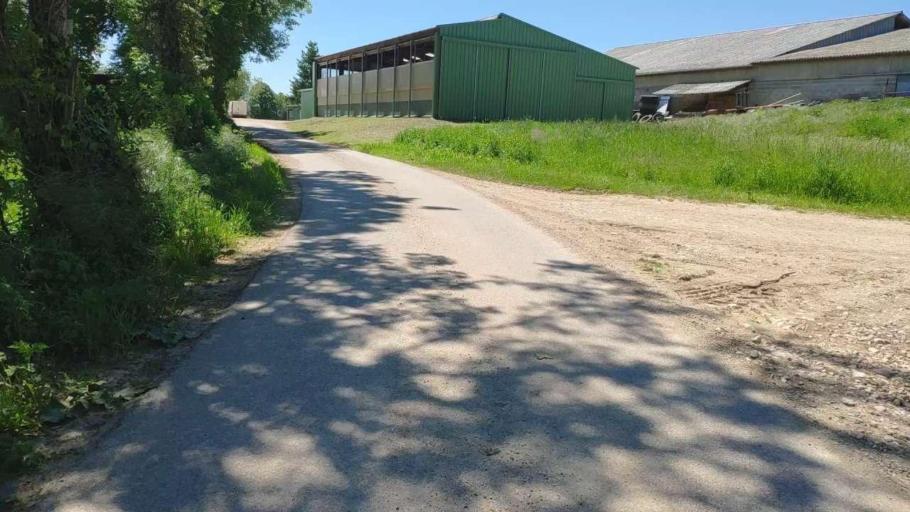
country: FR
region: Franche-Comte
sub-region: Departement du Jura
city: Perrigny
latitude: 46.7318
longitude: 5.6636
